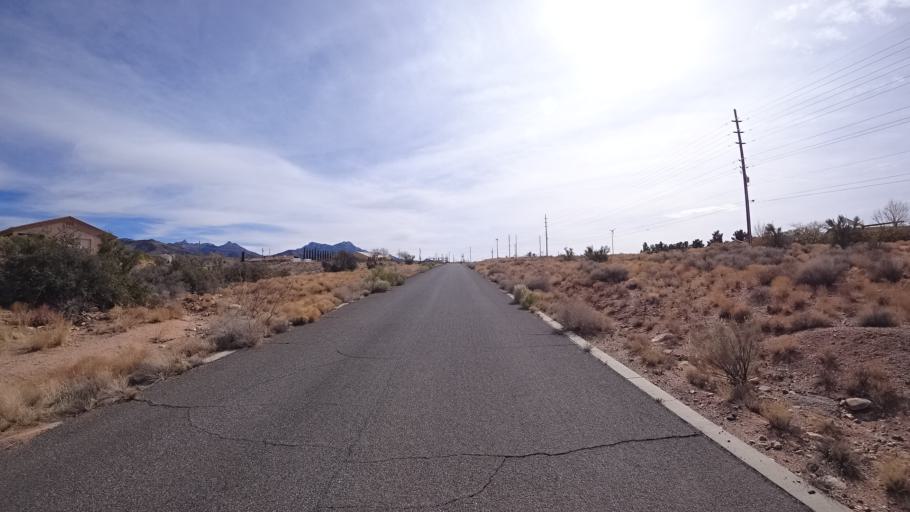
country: US
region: Arizona
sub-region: Mohave County
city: Kingman
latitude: 35.1835
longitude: -113.9828
